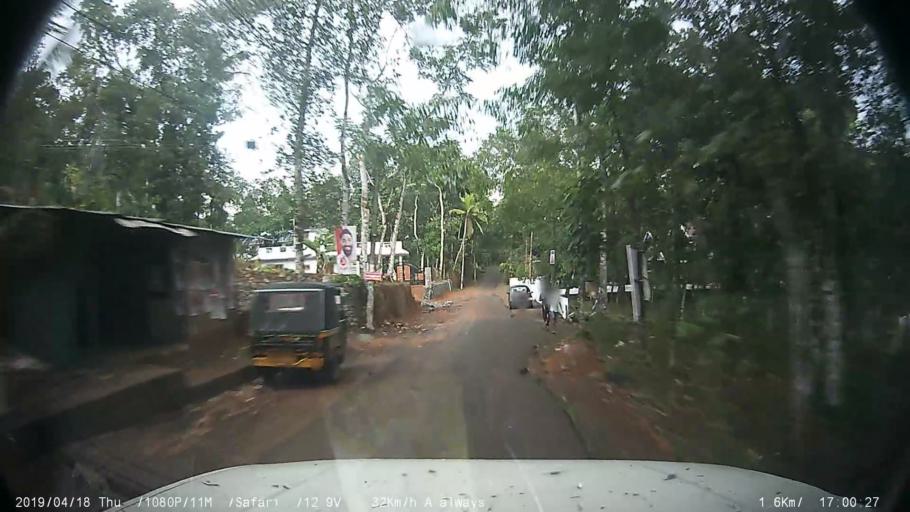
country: IN
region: Kerala
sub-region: Kottayam
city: Palackattumala
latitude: 9.7779
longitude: 76.5809
